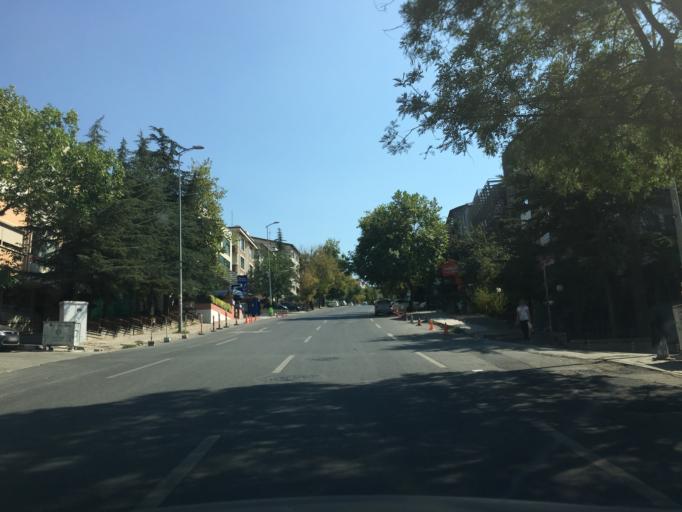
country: TR
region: Ankara
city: Cankaya
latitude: 39.8965
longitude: 32.8685
